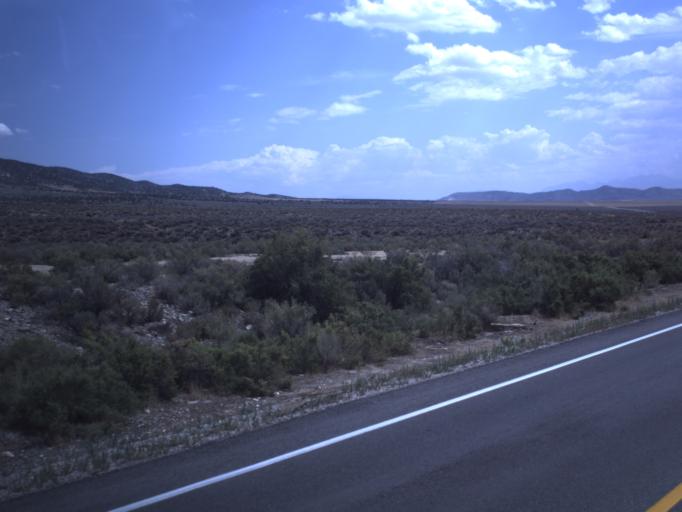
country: US
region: Utah
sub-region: Tooele County
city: Tooele
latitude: 40.2949
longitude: -112.2736
